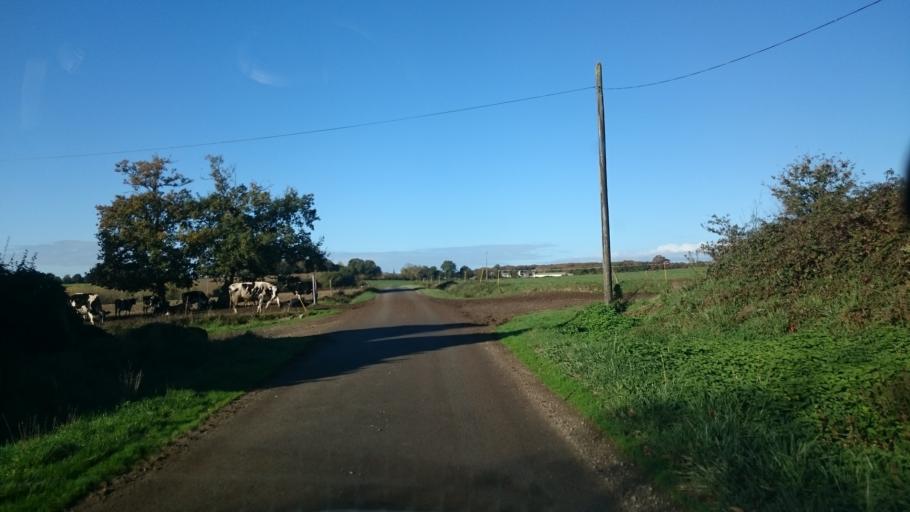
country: FR
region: Brittany
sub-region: Departement d'Ille-et-Vilaine
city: Crevin
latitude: 47.9472
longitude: -1.6948
